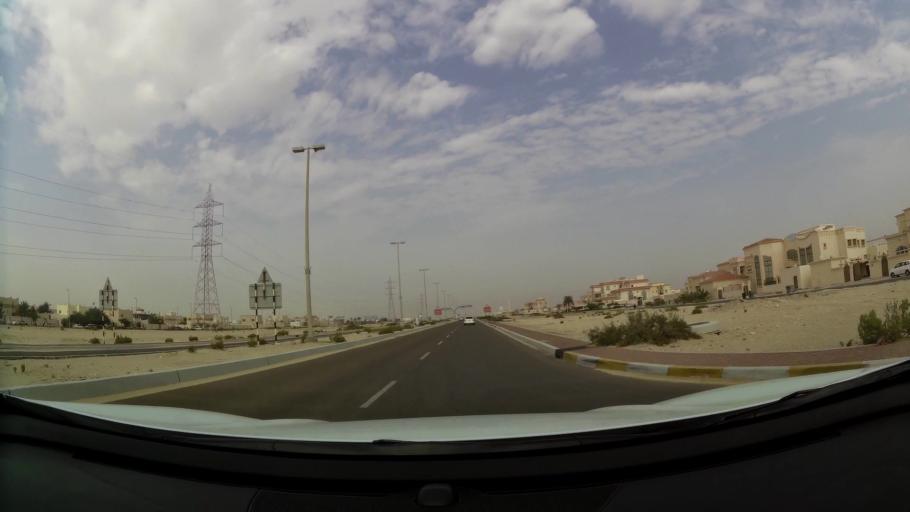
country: AE
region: Abu Dhabi
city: Abu Dhabi
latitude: 24.3087
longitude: 54.6457
